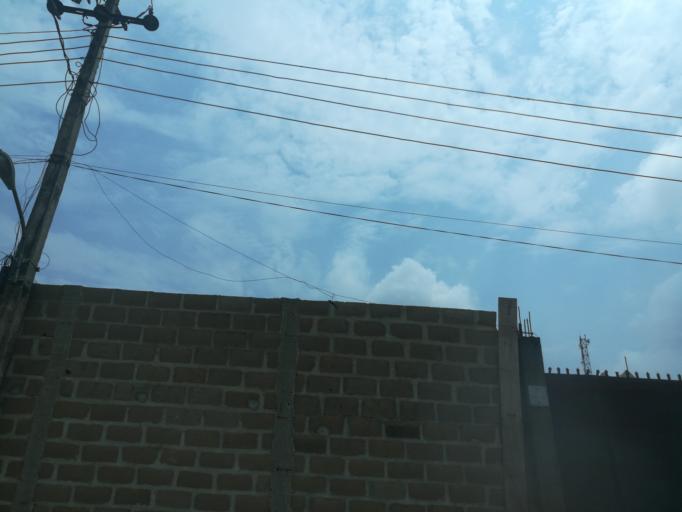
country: NG
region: Lagos
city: Ojota
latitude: 6.5880
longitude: 3.3637
